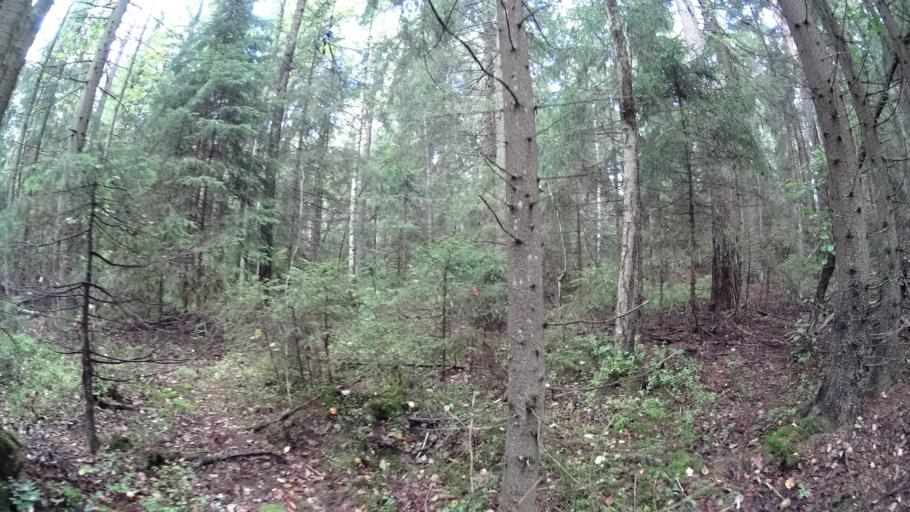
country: FI
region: Uusimaa
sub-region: Helsinki
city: Espoo
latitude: 60.2317
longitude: 24.6840
